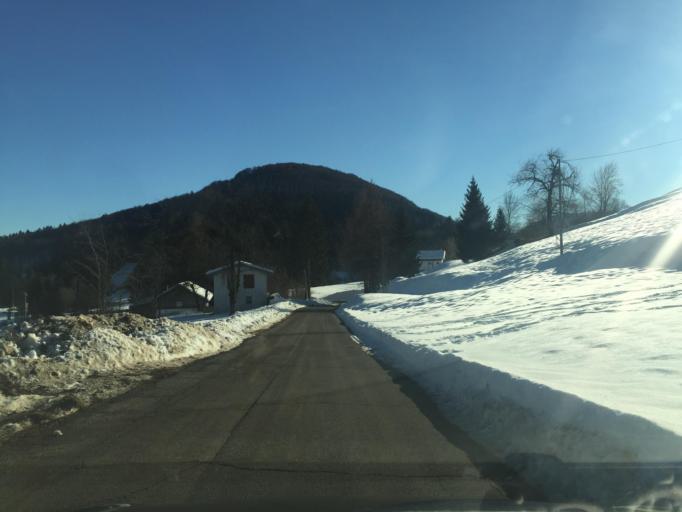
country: IT
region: Friuli Venezia Giulia
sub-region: Provincia di Udine
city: Chiaulis
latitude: 46.4278
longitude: 12.9772
